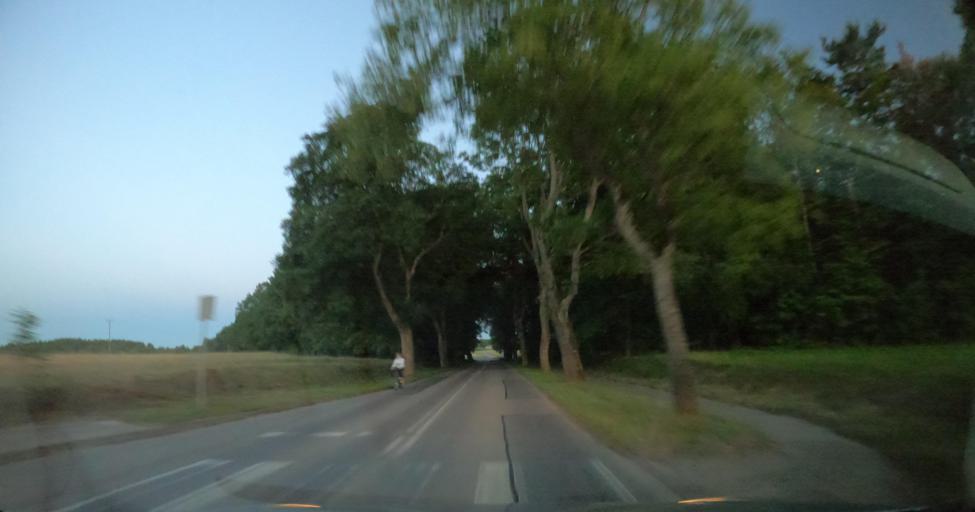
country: PL
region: Pomeranian Voivodeship
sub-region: Powiat wejherowski
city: Szemud
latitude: 54.4682
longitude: 18.2810
